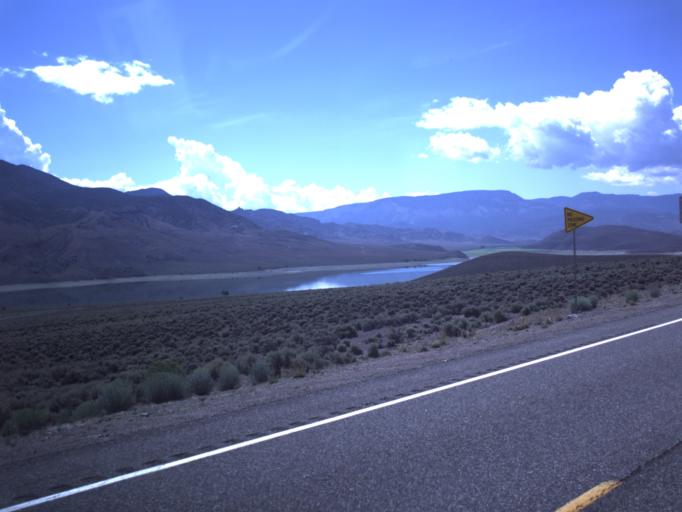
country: US
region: Utah
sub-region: Piute County
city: Junction
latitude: 38.3209
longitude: -112.2201
